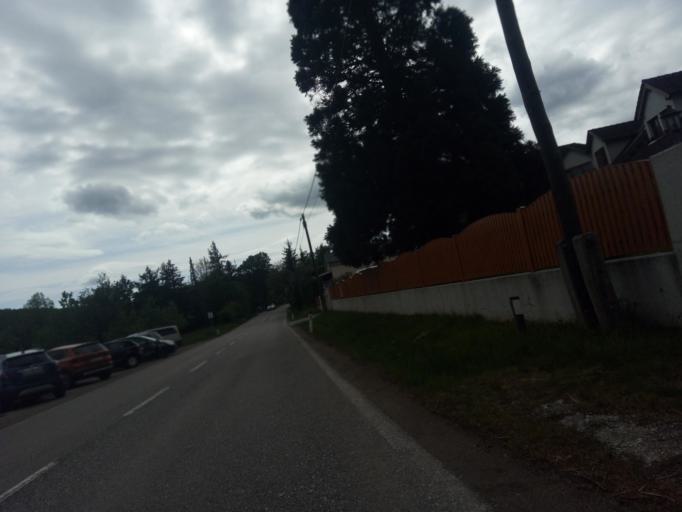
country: AT
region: Lower Austria
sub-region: Politischer Bezirk Wien-Umgebung
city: Wolfsgraben
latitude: 48.1354
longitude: 16.1227
